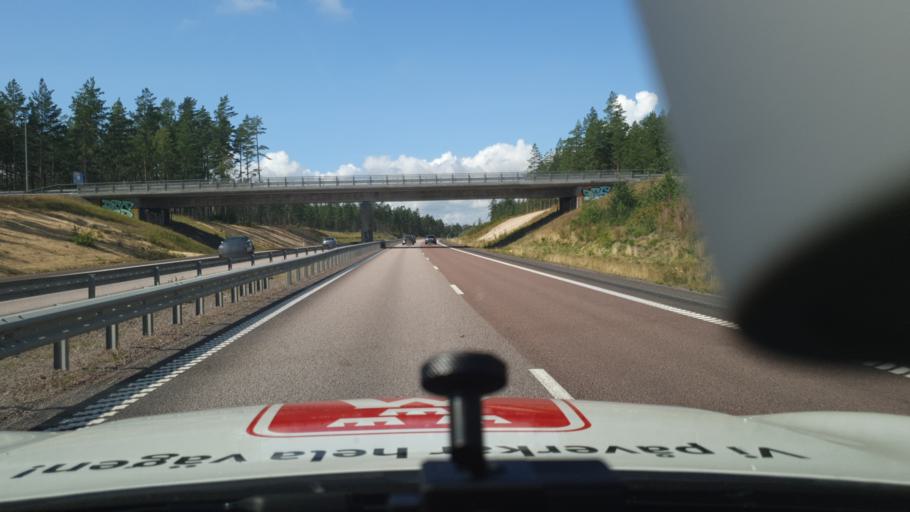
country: SE
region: Vaermland
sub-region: Kils Kommun
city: Kil
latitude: 59.3847
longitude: 13.3373
